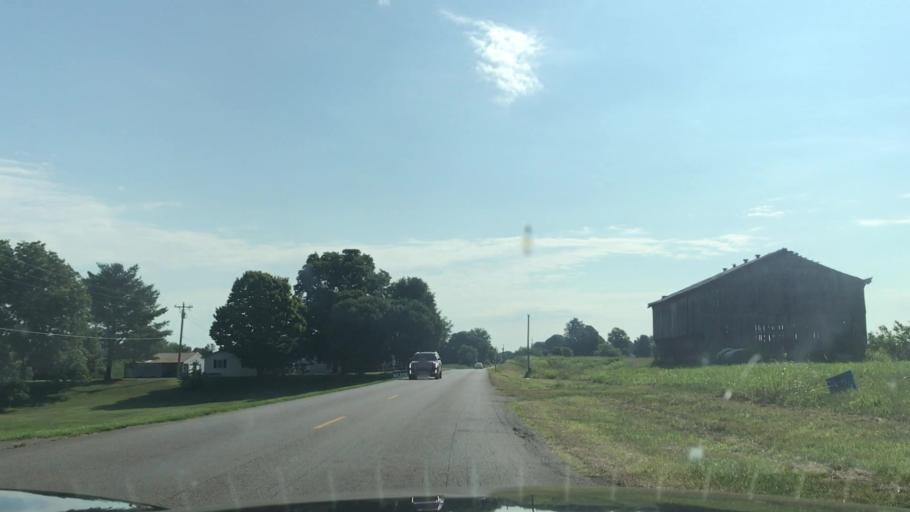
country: US
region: Kentucky
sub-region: Hart County
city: Horse Cave
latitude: 37.1768
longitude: -85.7872
